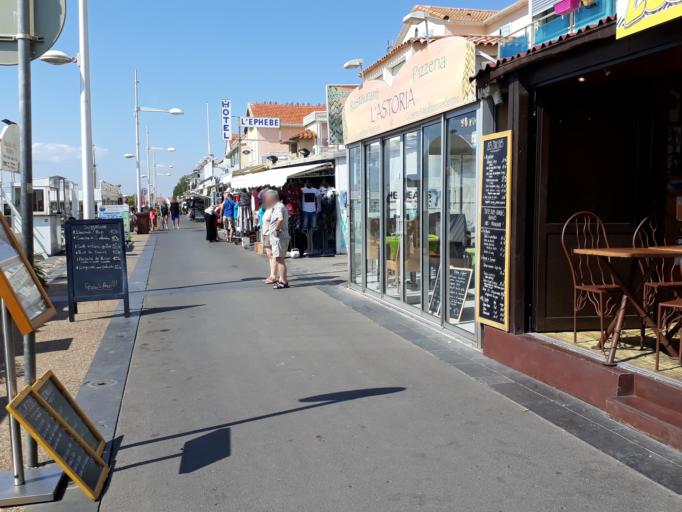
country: FR
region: Languedoc-Roussillon
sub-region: Departement de l'Herault
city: Vias
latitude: 43.2839
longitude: 3.4448
